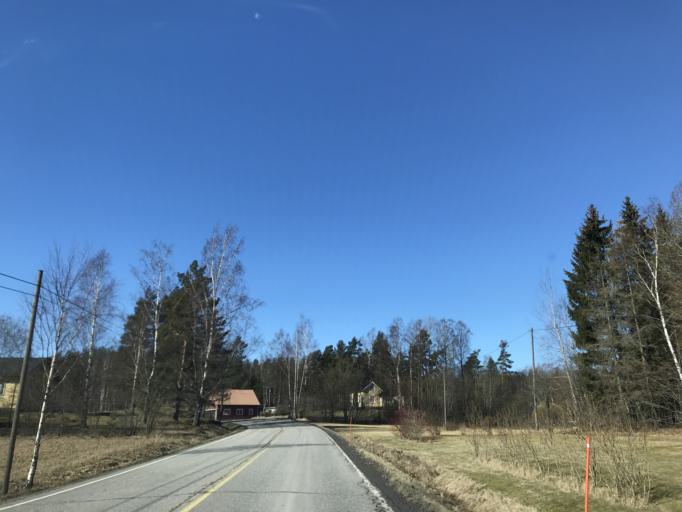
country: FI
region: Uusimaa
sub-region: Raaseporin
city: Pohja
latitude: 60.0930
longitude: 23.4697
